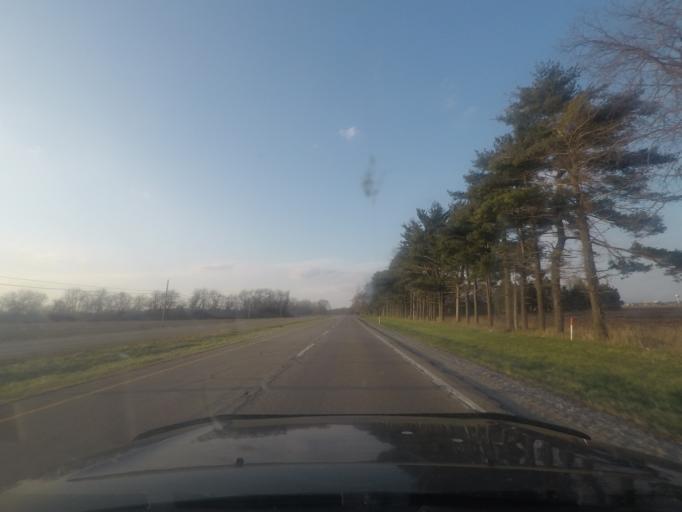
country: US
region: Indiana
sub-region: LaPorte County
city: LaPorte
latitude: 41.5787
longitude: -86.7002
